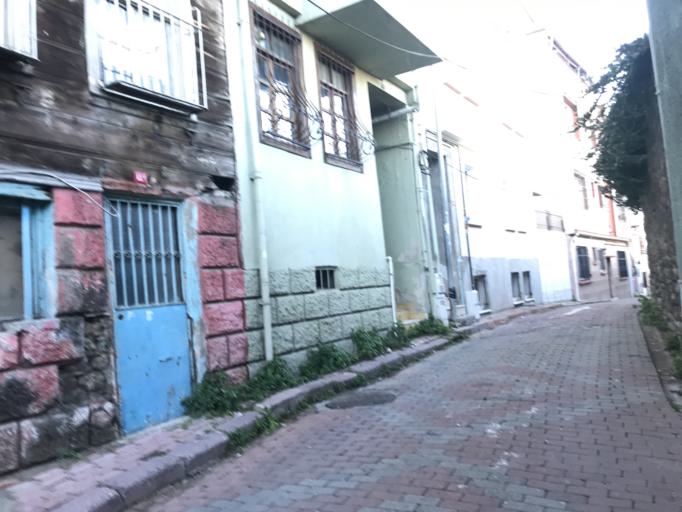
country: TR
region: Istanbul
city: Istanbul
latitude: 41.0284
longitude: 28.9519
